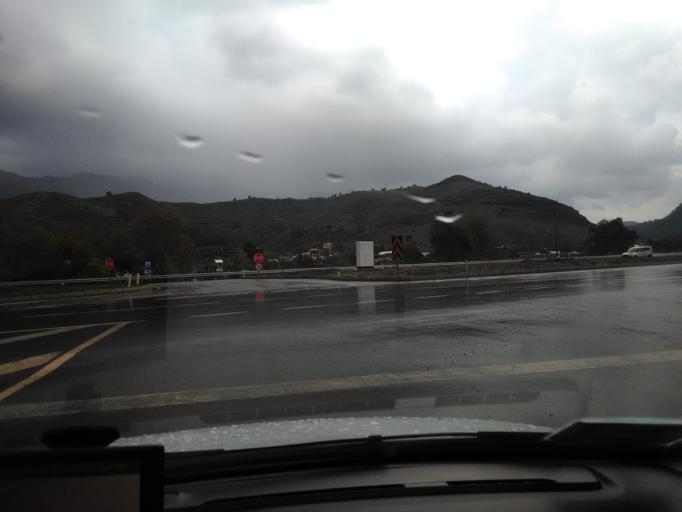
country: TR
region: Antalya
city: Gazipasa
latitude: 36.1691
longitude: 32.4452
